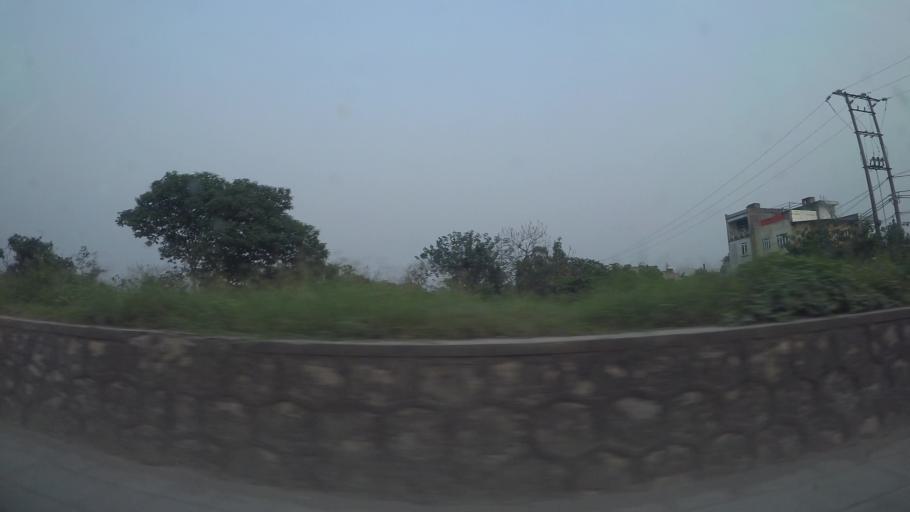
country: VN
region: Ha Noi
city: Van Dien
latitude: 20.9742
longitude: 105.8883
